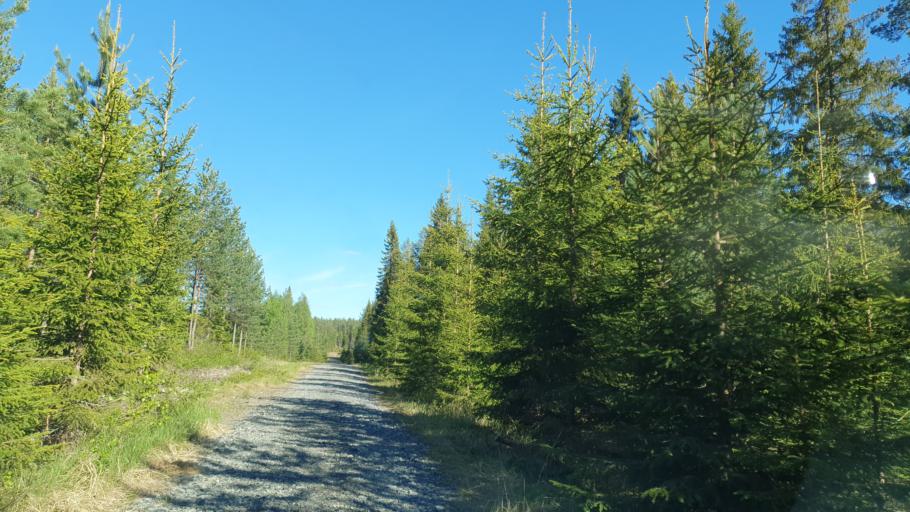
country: FI
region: Kainuu
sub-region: Kehys-Kainuu
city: Kuhmo
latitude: 64.1796
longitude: 29.4180
